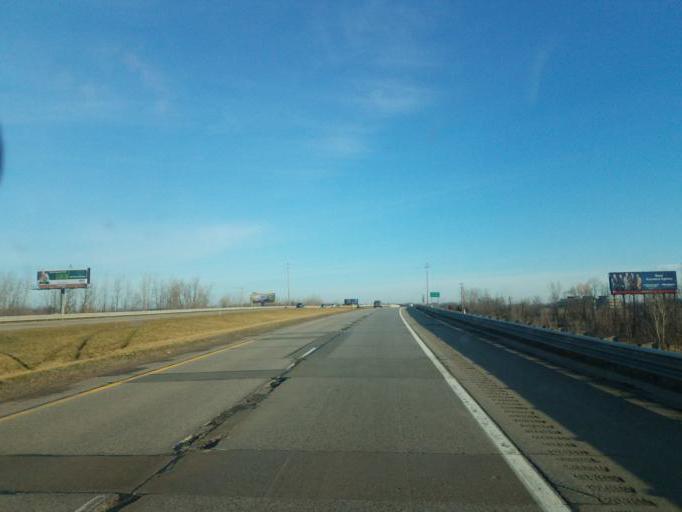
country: US
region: Michigan
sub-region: Ingham County
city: East Lansing
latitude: 42.7696
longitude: -84.5129
